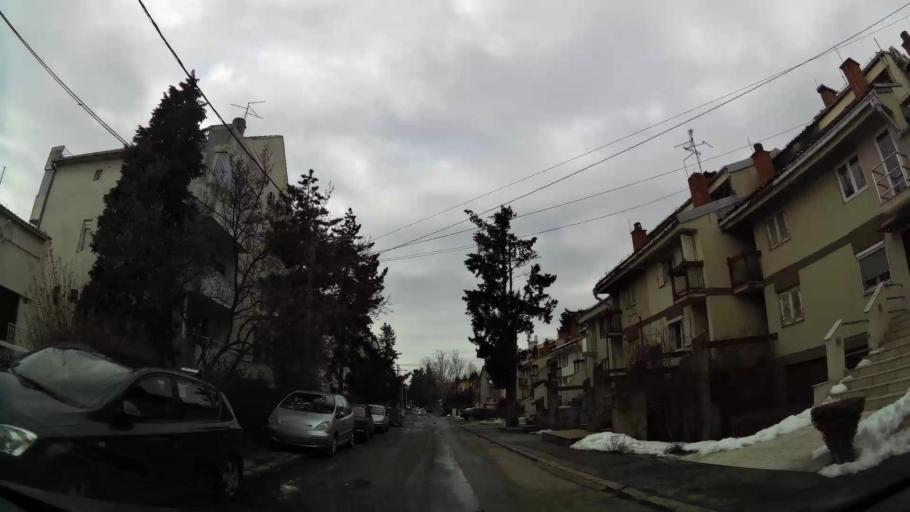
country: RS
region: Central Serbia
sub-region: Belgrade
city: Rakovica
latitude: 44.7485
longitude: 20.4094
